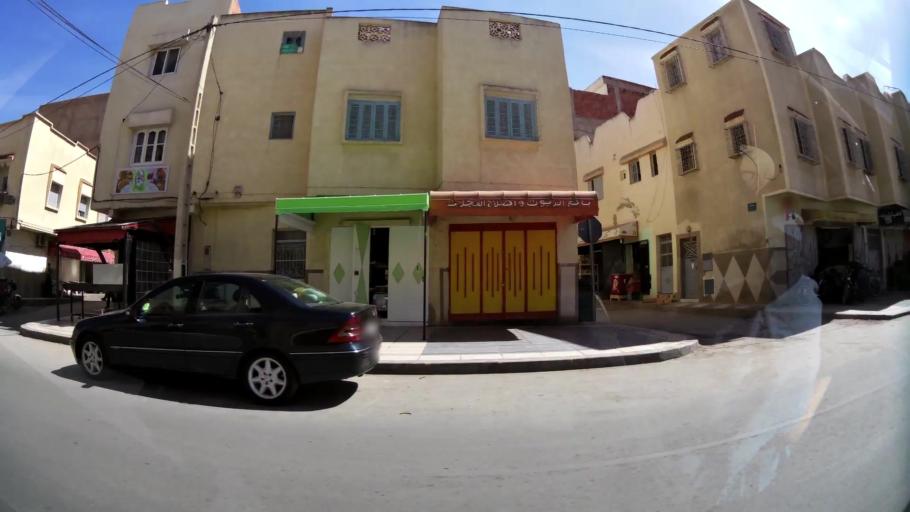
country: MA
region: Oriental
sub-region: Oujda-Angad
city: Oujda
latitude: 34.6566
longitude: -1.9036
